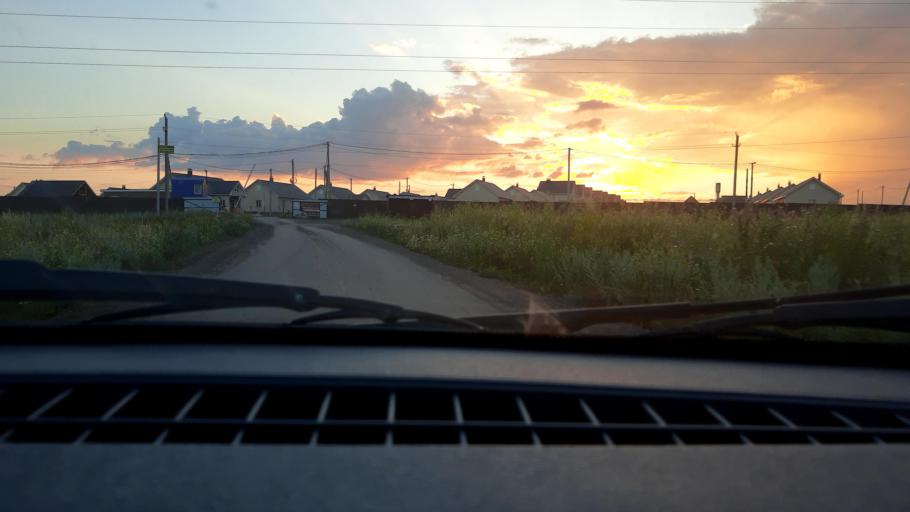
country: RU
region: Bashkortostan
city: Mikhaylovka
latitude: 54.7840
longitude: 55.8045
